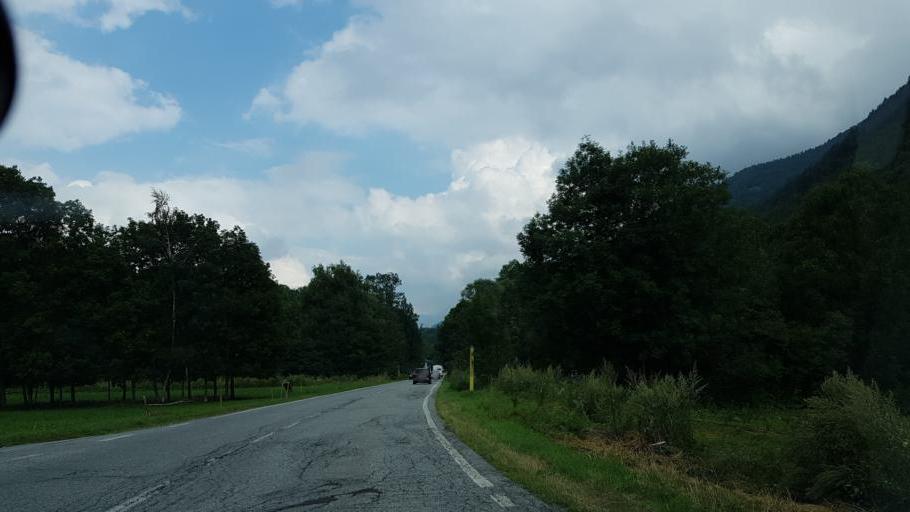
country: IT
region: Piedmont
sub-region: Provincia di Cuneo
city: Sampeyre
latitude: 44.5806
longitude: 7.1509
